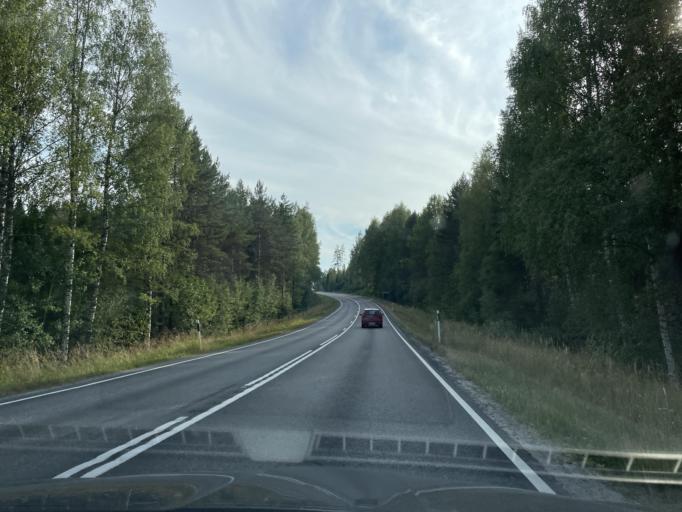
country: FI
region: Central Finland
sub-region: Jaemsae
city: Kuhmoinen
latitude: 61.6069
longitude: 25.2507
